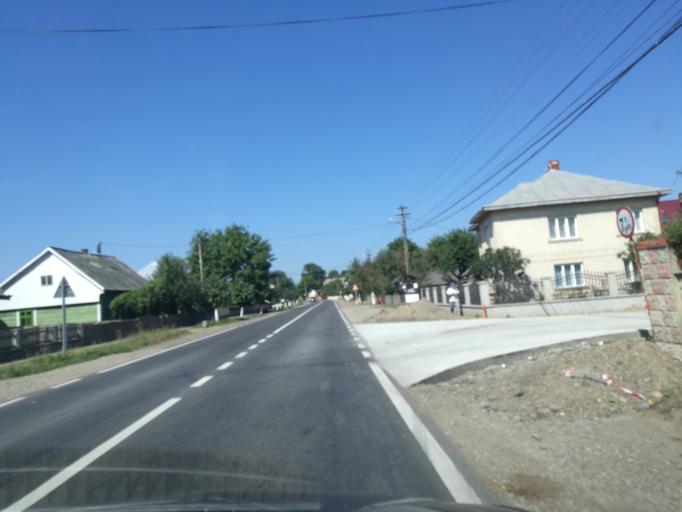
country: RO
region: Suceava
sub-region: Comuna Milisauti
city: Badeuti
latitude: 47.8021
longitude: 25.9861
